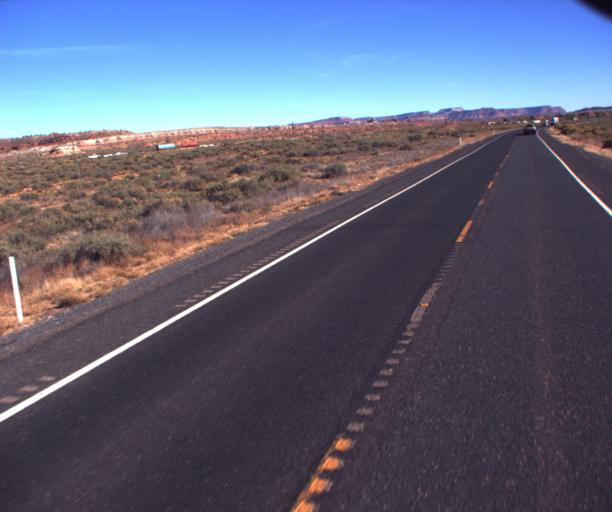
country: US
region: Arizona
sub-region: Coconino County
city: Fredonia
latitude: 36.9405
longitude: -112.5478
